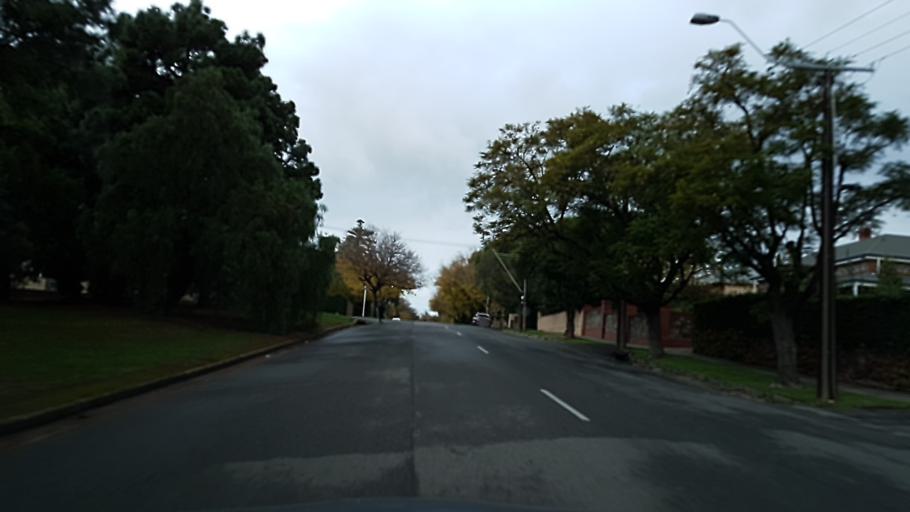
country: AU
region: South Australia
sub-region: Adelaide
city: North Adelaide
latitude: -34.9071
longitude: 138.5841
